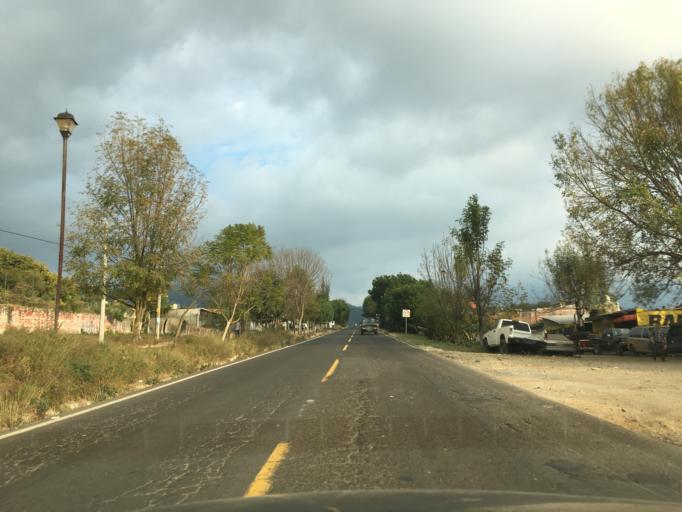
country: MX
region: Michoacan
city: Tingambato
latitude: 19.5071
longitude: -101.8549
